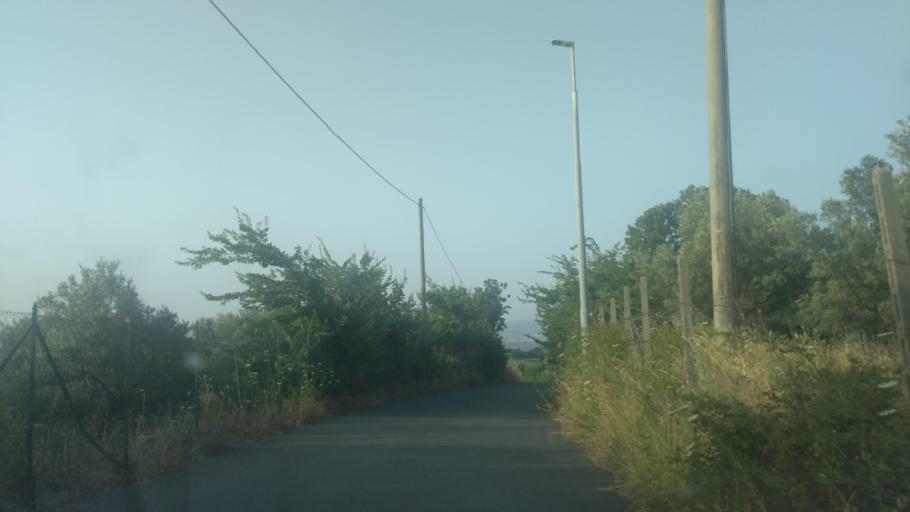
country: IT
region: Calabria
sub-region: Provincia di Catanzaro
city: Staletti
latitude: 38.7606
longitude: 16.5337
